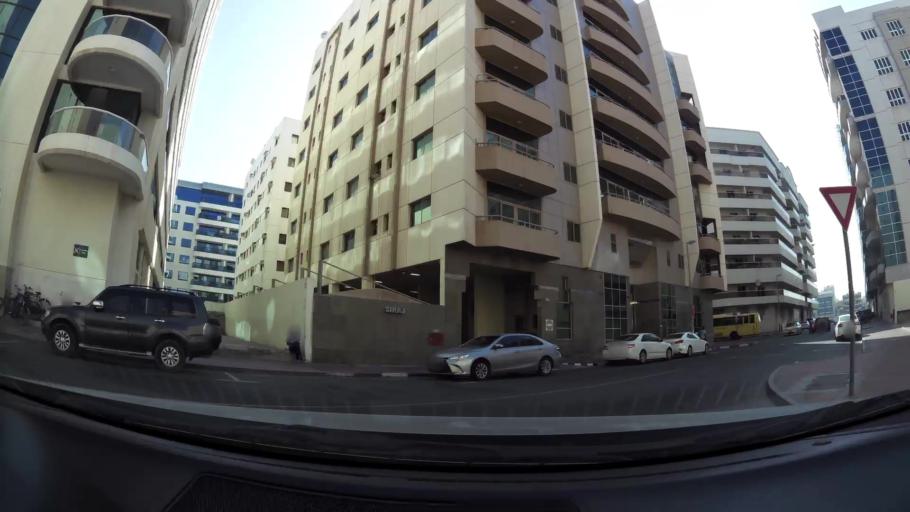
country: AE
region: Ash Shariqah
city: Sharjah
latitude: 25.2497
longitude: 55.2978
